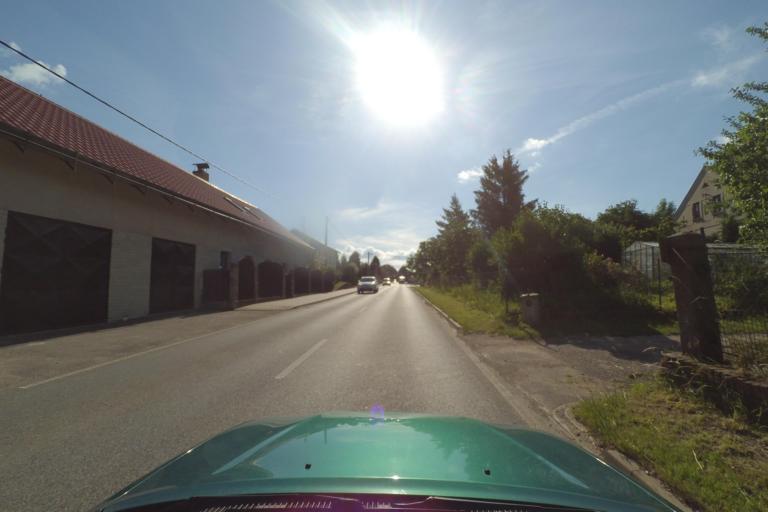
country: CZ
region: Kralovehradecky
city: Dvur Kralove nad Labem
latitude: 50.4309
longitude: 15.8465
